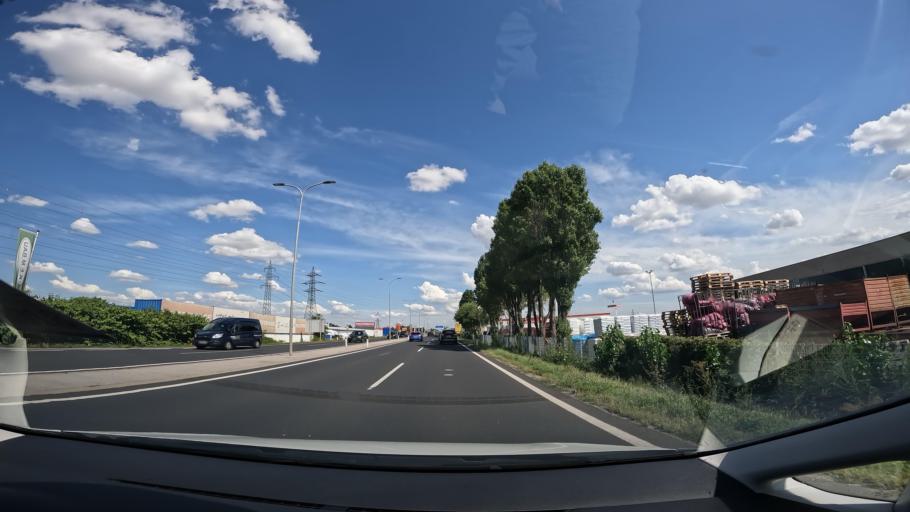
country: AT
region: Lower Austria
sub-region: Politischer Bezirk Modling
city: Wiener Neudorf
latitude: 48.0794
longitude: 16.3279
